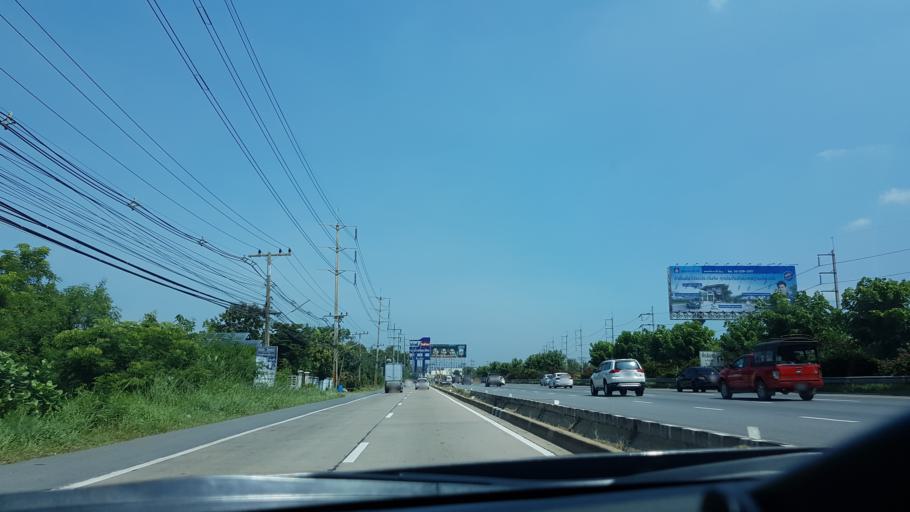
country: TH
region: Sara Buri
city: Nong Khae
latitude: 14.3631
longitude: 100.8772
